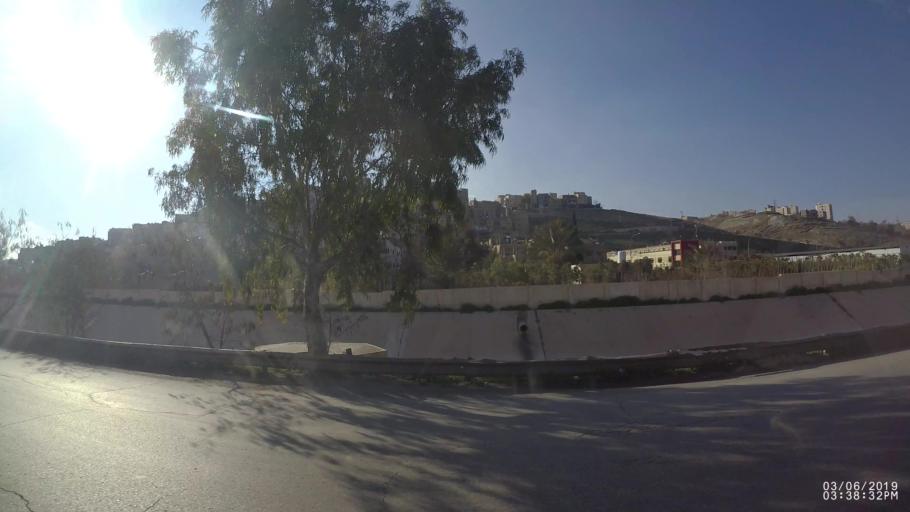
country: JO
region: Amman
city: Amman
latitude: 31.9724
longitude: 35.9713
